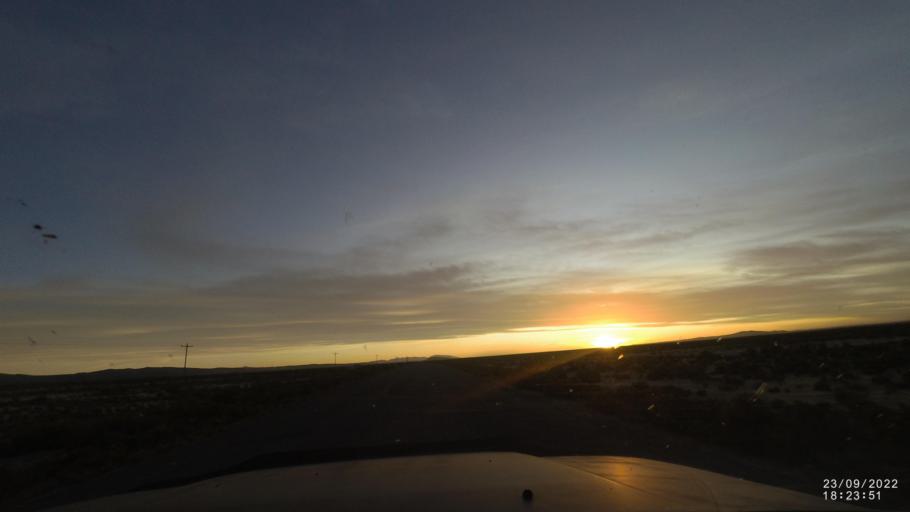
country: BO
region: Oruro
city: Challapata
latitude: -19.2982
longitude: -67.1105
